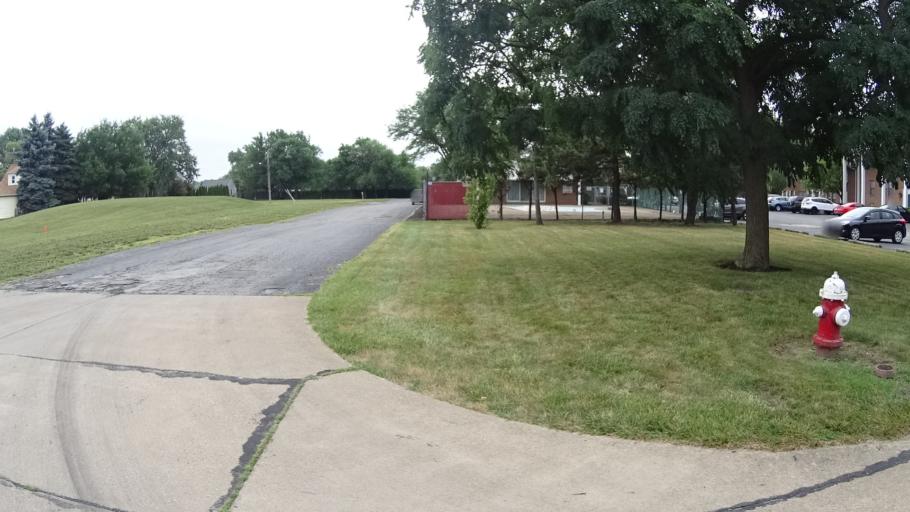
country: US
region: Ohio
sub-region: Erie County
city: Sandusky
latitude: 41.4420
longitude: -82.6926
